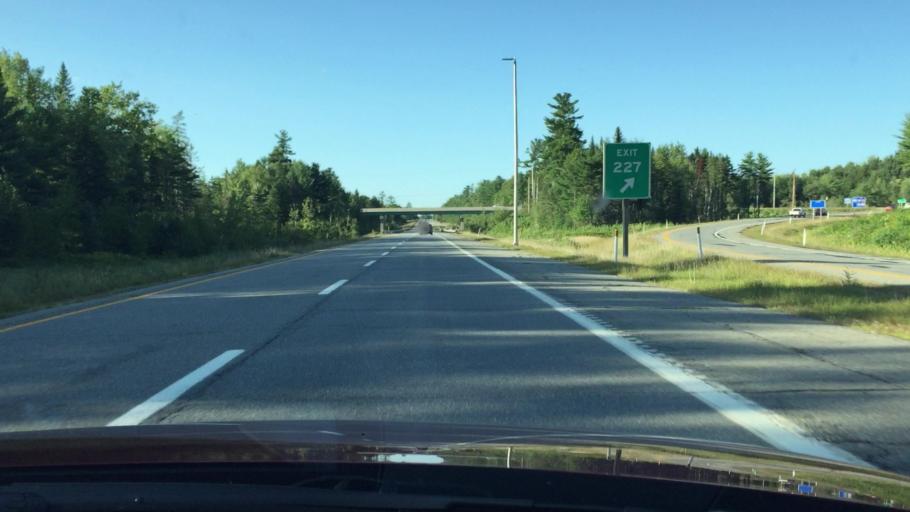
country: US
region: Maine
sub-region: Penobscot County
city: Lincoln
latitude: 45.3728
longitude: -68.6047
